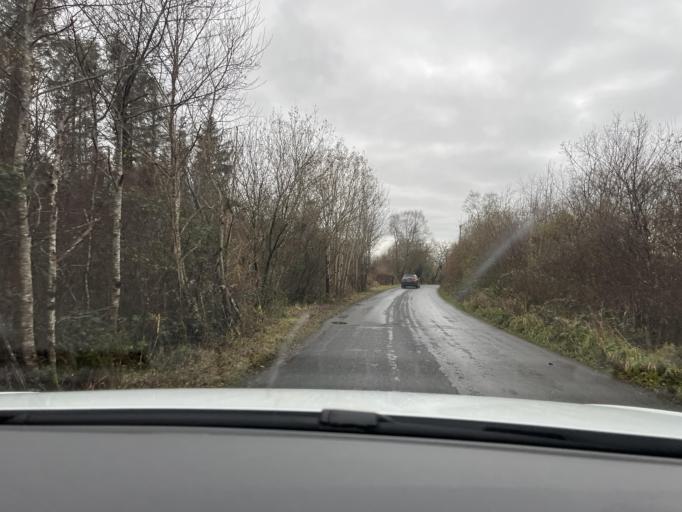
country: IE
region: Connaught
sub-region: County Leitrim
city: Manorhamilton
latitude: 54.2659
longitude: -8.2261
